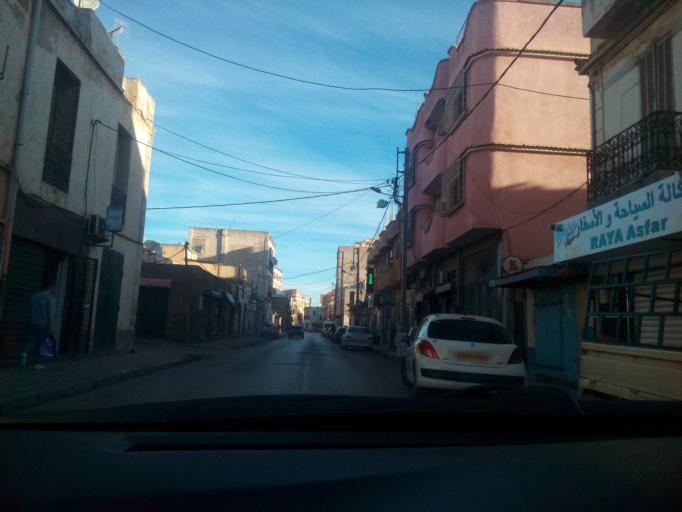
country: DZ
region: Oran
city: Oran
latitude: 35.6880
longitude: -0.6558
